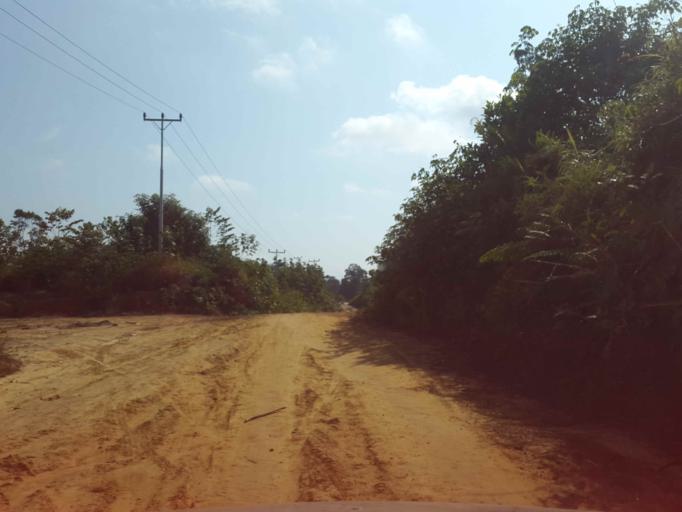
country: MY
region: Sarawak
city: Simanggang
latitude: 0.9375
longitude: 111.0915
